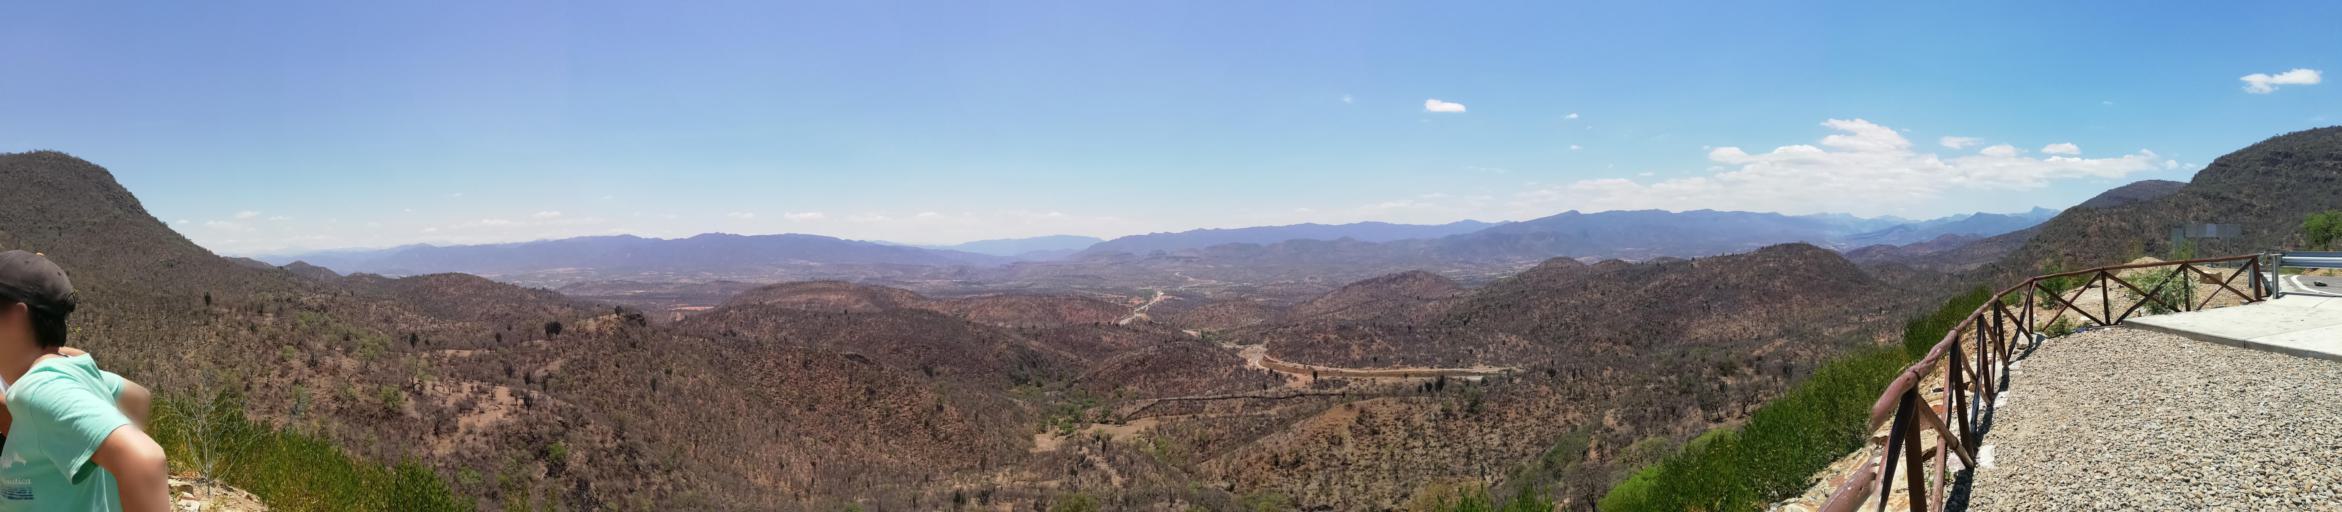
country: BO
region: Cochabamba
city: Aiquile
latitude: -18.1847
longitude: -64.9131
